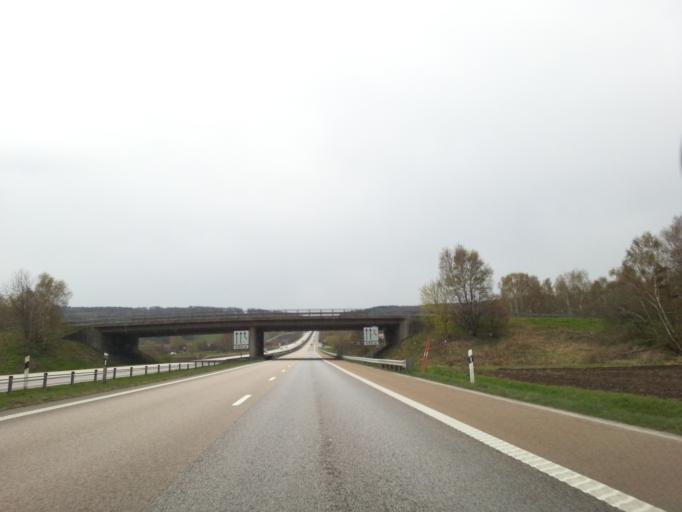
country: SE
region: Halland
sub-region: Laholms Kommun
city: Mellbystrand
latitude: 56.4283
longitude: 12.9516
